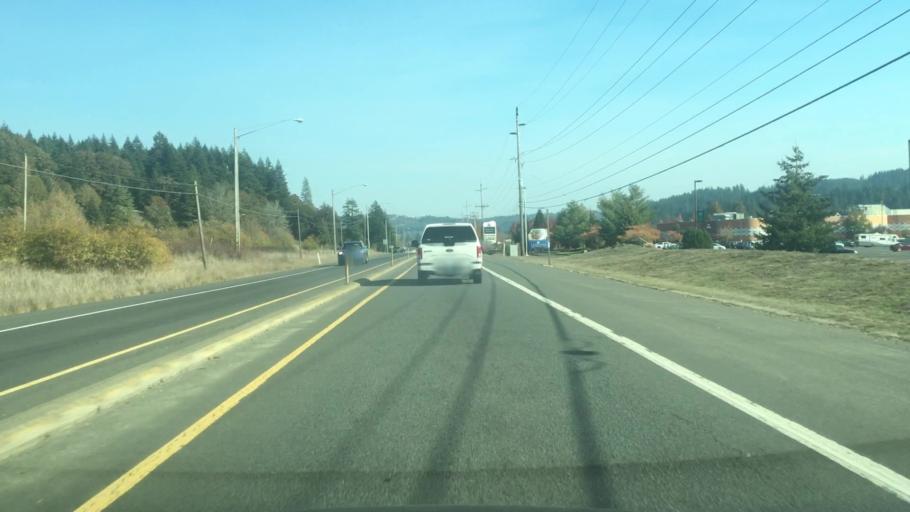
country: US
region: Oregon
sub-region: Polk County
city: Grand Ronde
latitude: 45.0596
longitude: -123.5857
